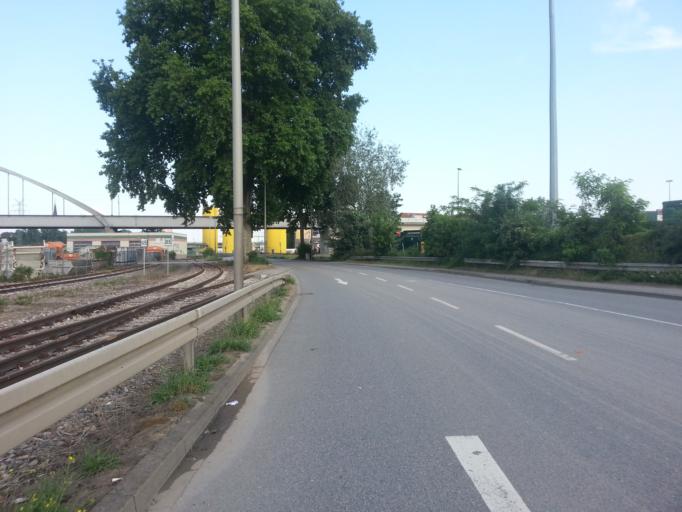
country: DE
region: Rheinland-Pfalz
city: Ludwigshafen am Rhein
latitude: 49.4998
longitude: 8.4541
